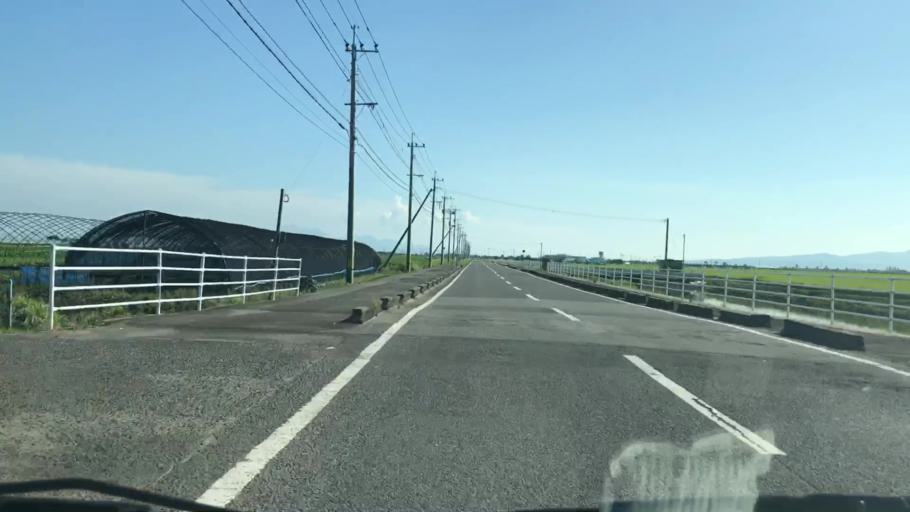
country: JP
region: Saga Prefecture
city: Okawa
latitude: 33.1731
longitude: 130.3111
